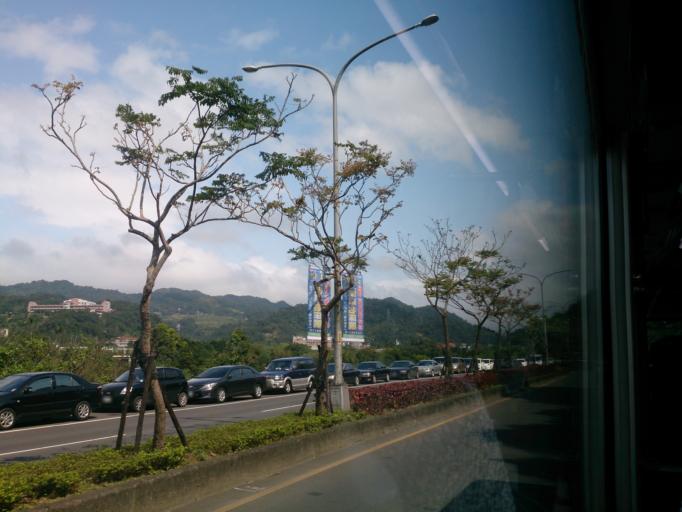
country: TW
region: Taipei
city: Taipei
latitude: 25.0084
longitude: 121.6356
